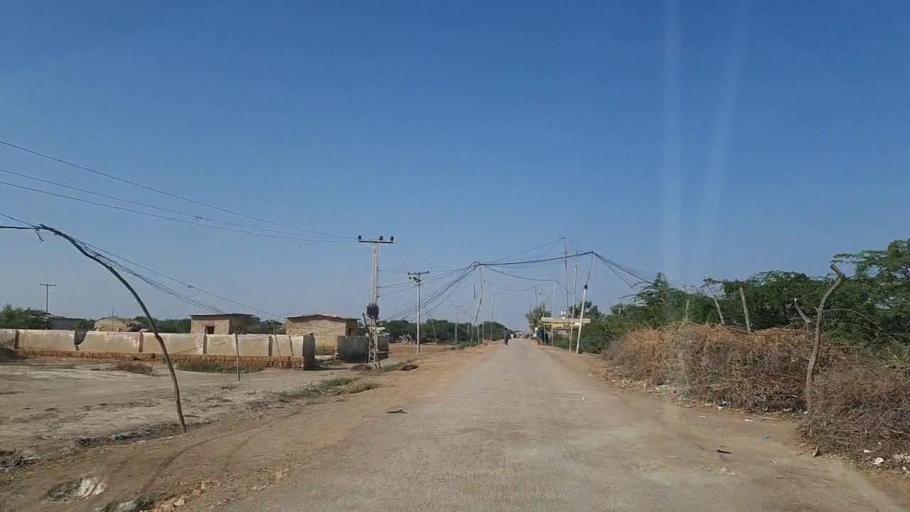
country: PK
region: Sindh
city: Thatta
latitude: 24.6169
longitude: 68.0286
